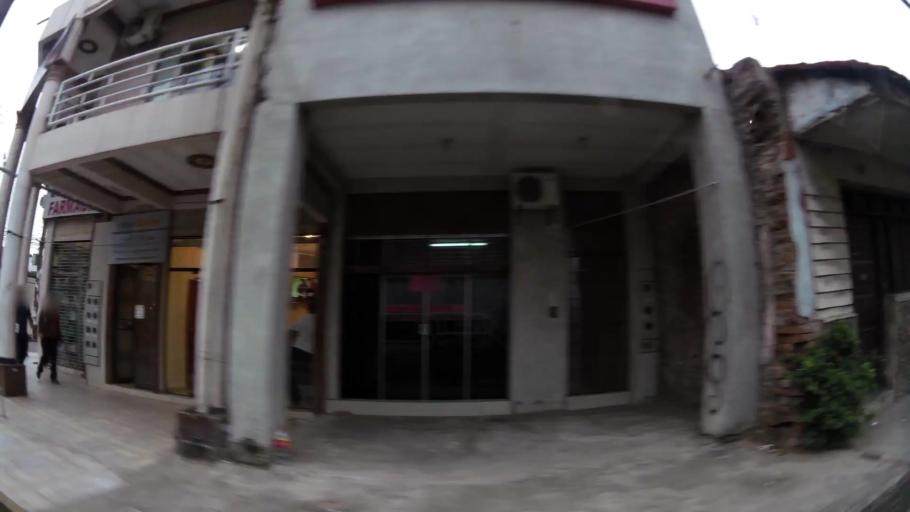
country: BO
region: Santa Cruz
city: Santa Cruz de la Sierra
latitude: -17.7801
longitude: -63.1850
